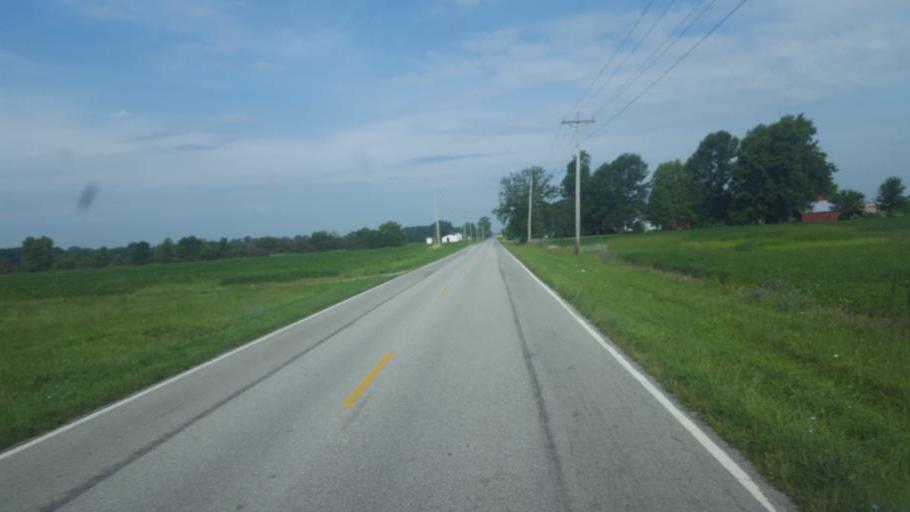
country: US
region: Ohio
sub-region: Marion County
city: Marion
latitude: 40.5642
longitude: -83.2371
